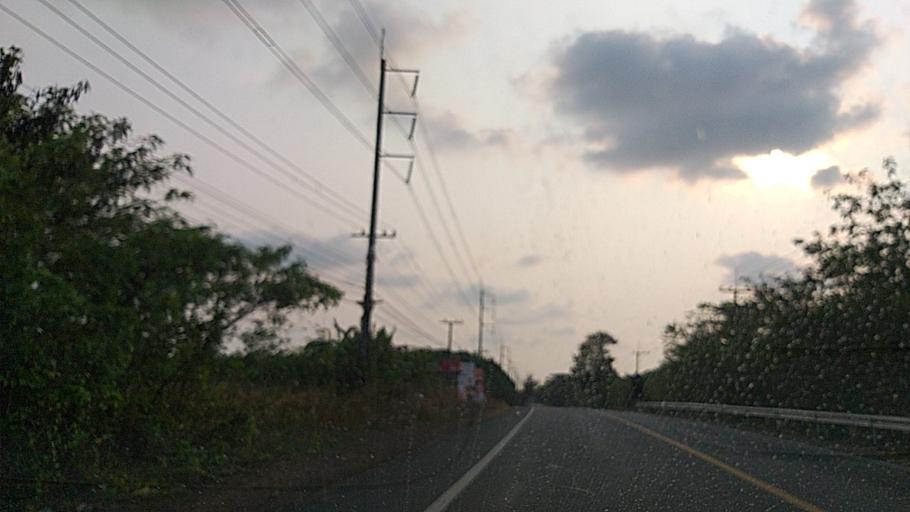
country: TH
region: Trat
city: Laem Ngop
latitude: 12.2636
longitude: 102.2994
